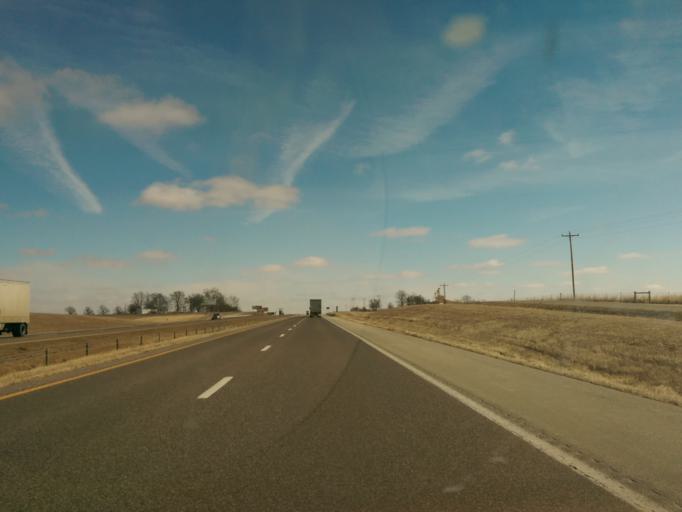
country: US
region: Missouri
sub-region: Callaway County
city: Fulton
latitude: 38.9439
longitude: -91.9070
